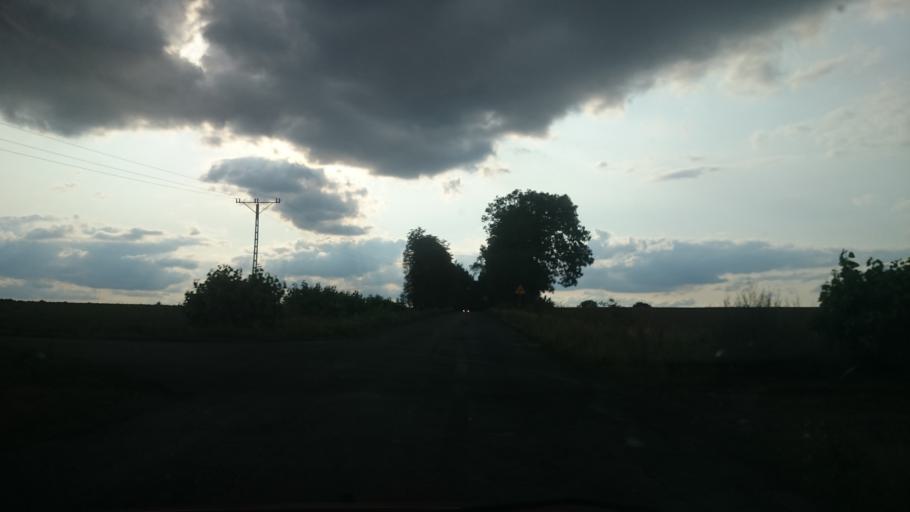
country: PL
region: Opole Voivodeship
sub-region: Powiat nyski
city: Otmuchow
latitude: 50.4991
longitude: 17.2247
